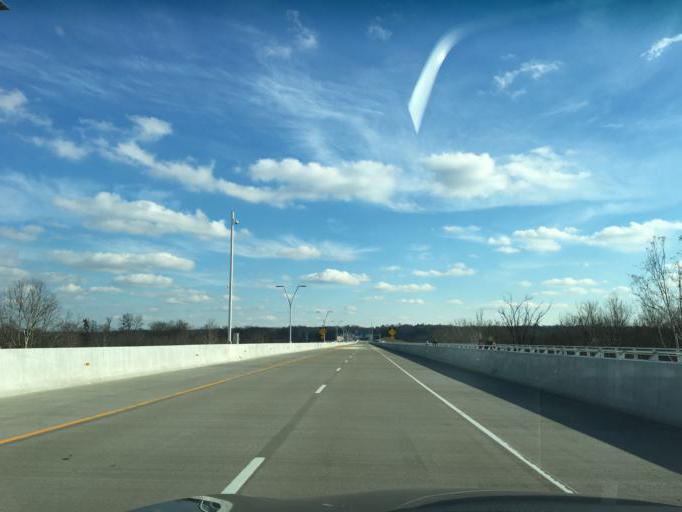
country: US
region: Kentucky
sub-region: Jefferson County
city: Prospect
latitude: 38.3398
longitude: -85.6400
